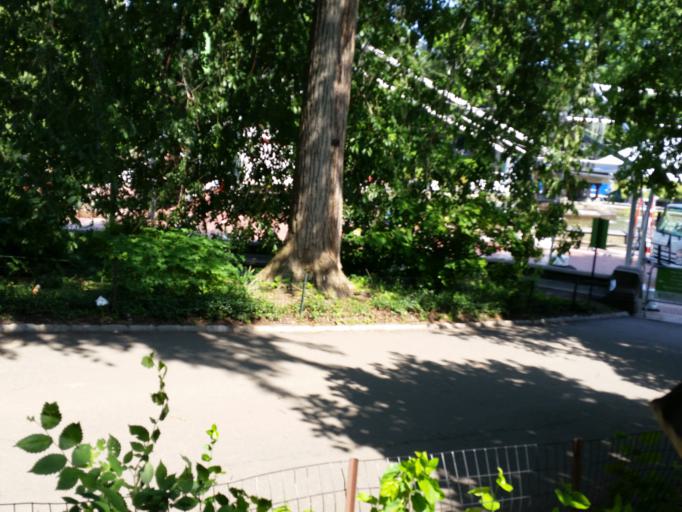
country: US
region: New York
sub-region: New York County
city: Manhattan
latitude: 40.7745
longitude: -73.9713
